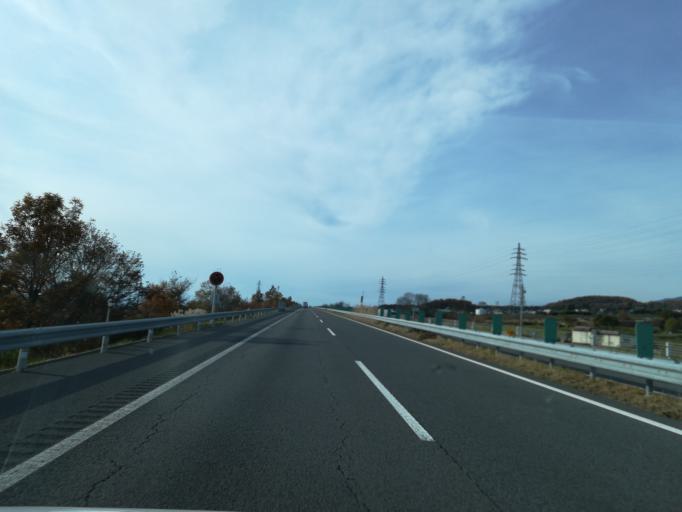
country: JP
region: Nagano
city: Komoro
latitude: 36.3268
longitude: 138.4629
